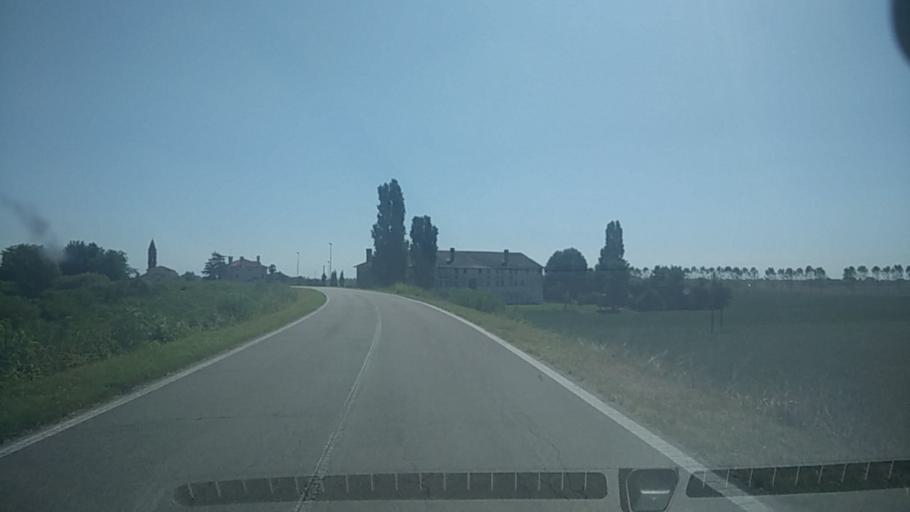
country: IT
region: Veneto
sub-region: Provincia di Venezia
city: La Salute di Livenza
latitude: 45.6453
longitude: 12.8199
